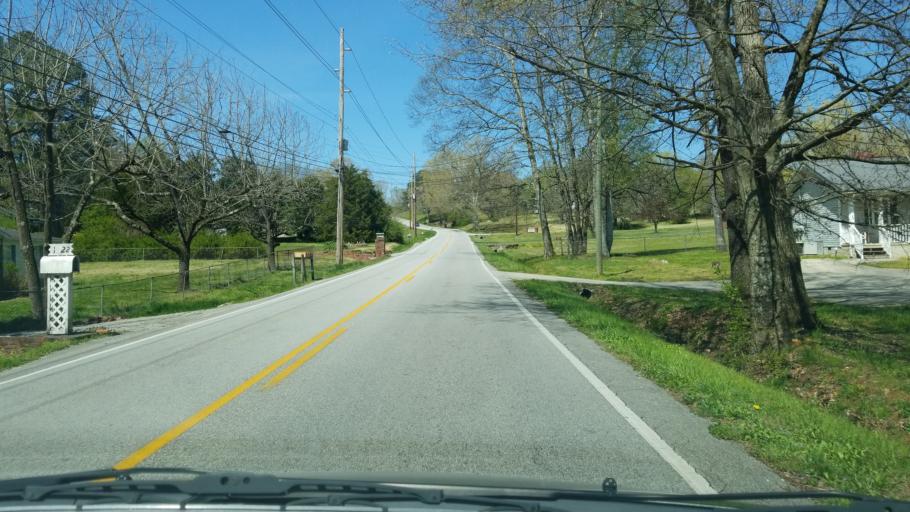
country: US
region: Tennessee
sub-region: Hamilton County
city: Middle Valley
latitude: 35.1931
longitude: -85.1942
